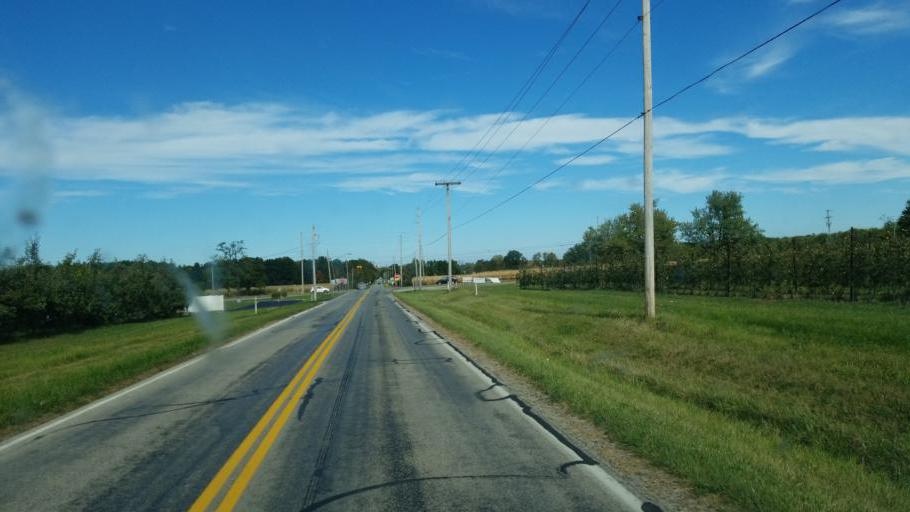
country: US
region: Ohio
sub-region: Huron County
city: Wakeman
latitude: 41.3033
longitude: -82.4928
